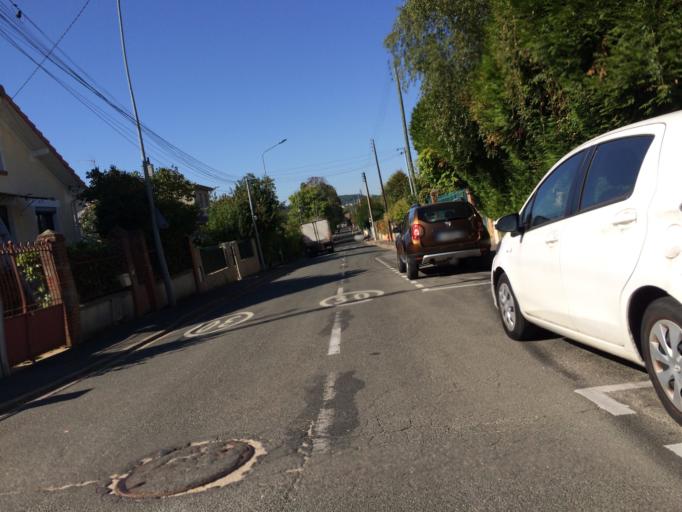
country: FR
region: Ile-de-France
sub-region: Departement de l'Essonne
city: Orsay
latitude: 48.7041
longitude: 2.2067
